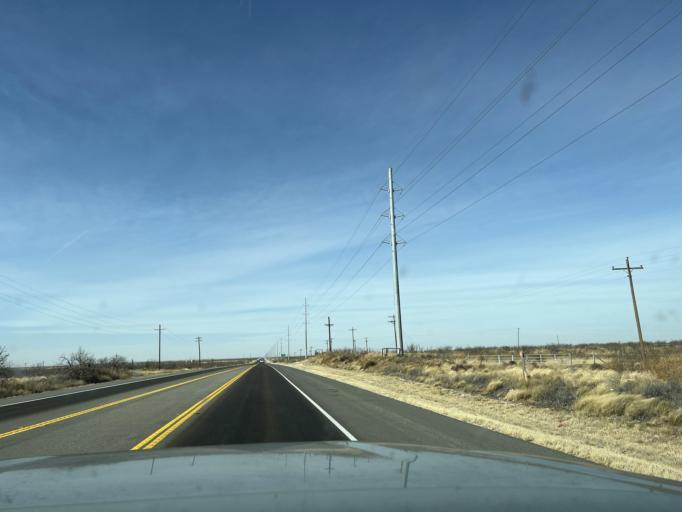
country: US
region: Texas
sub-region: Andrews County
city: Andrews
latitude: 32.3343
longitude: -102.6592
